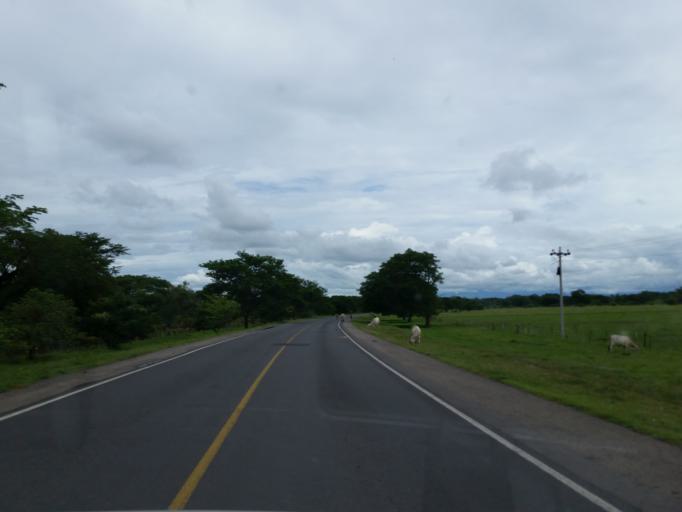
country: NI
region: Chinandega
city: Somotillo
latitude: 12.8335
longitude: -86.8941
